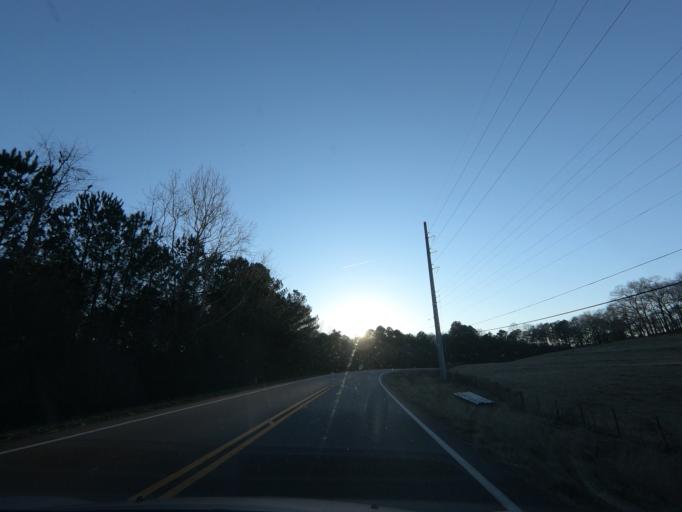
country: US
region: Georgia
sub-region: Dawson County
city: Dawsonville
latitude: 34.3494
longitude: -84.1070
